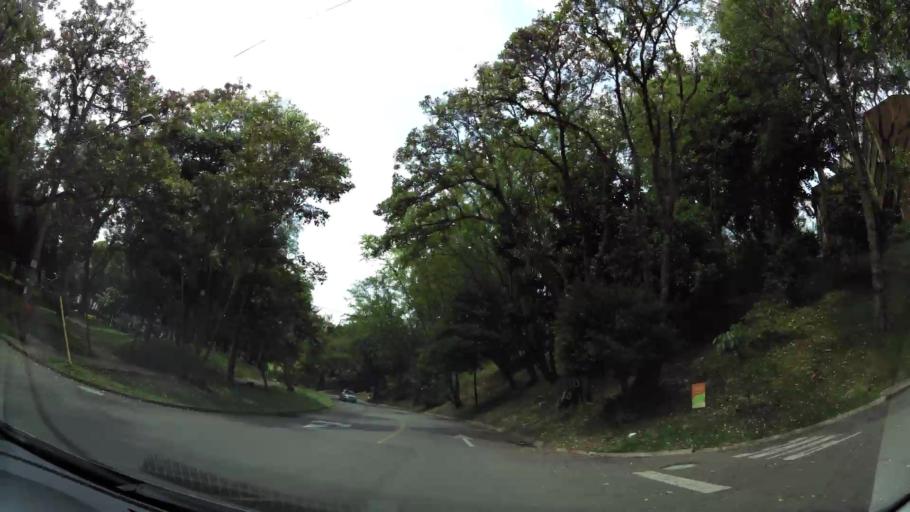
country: CO
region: Antioquia
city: Medellin
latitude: 6.2492
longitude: -75.6160
